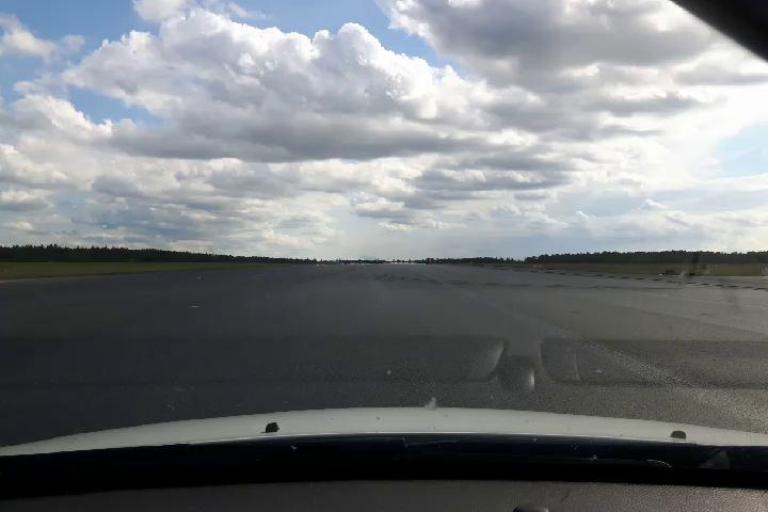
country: SE
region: Stockholm
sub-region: Sigtuna Kommun
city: Rosersberg
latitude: 59.6288
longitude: 17.9515
